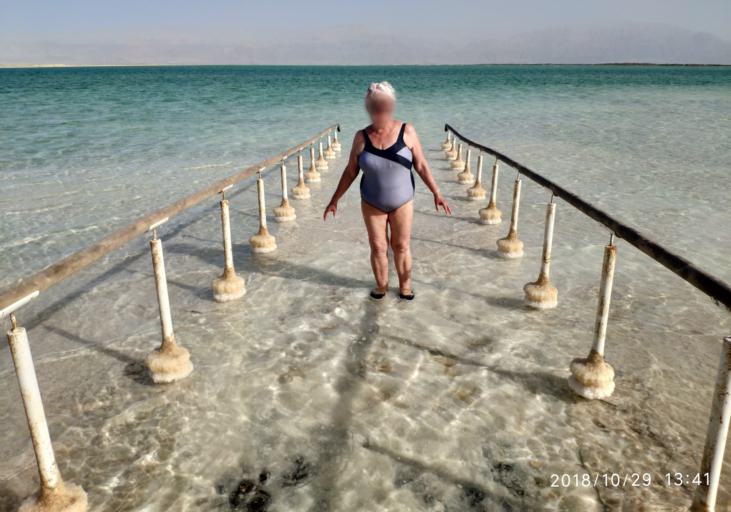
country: IL
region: Southern District
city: `En Boqeq
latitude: 31.1745
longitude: 35.3694
